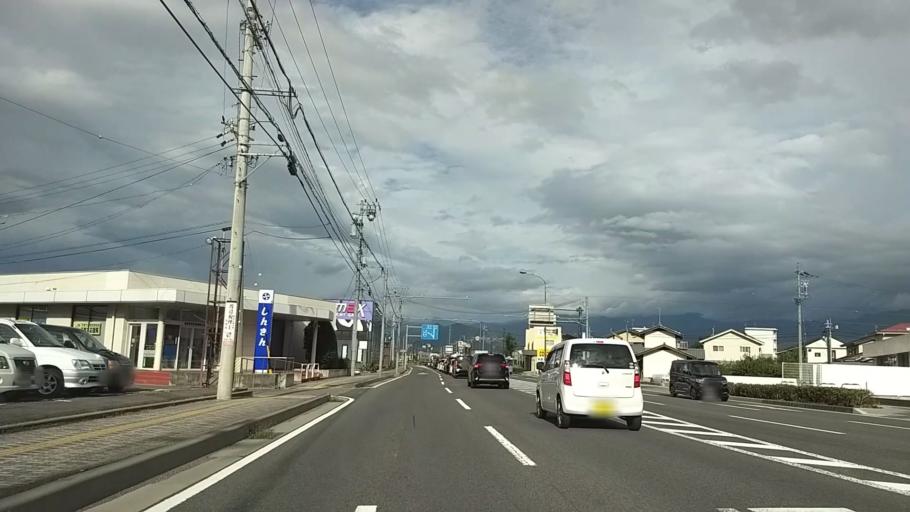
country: JP
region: Nagano
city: Suzaka
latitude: 36.6611
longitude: 138.2583
